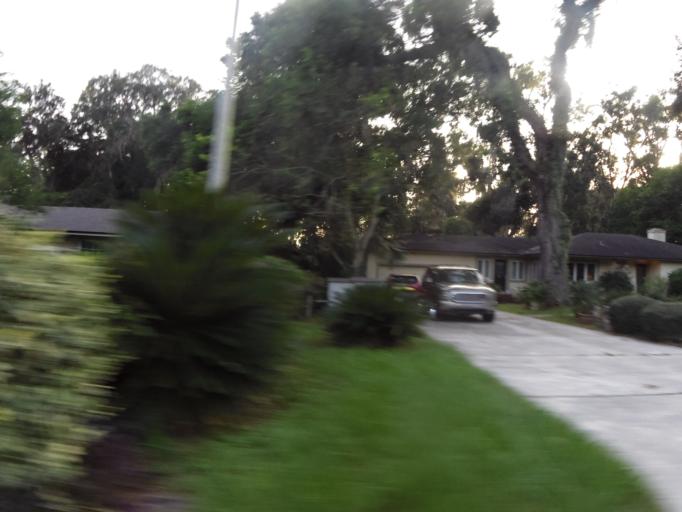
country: US
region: Florida
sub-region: Clay County
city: Orange Park
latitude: 30.2024
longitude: -81.6378
